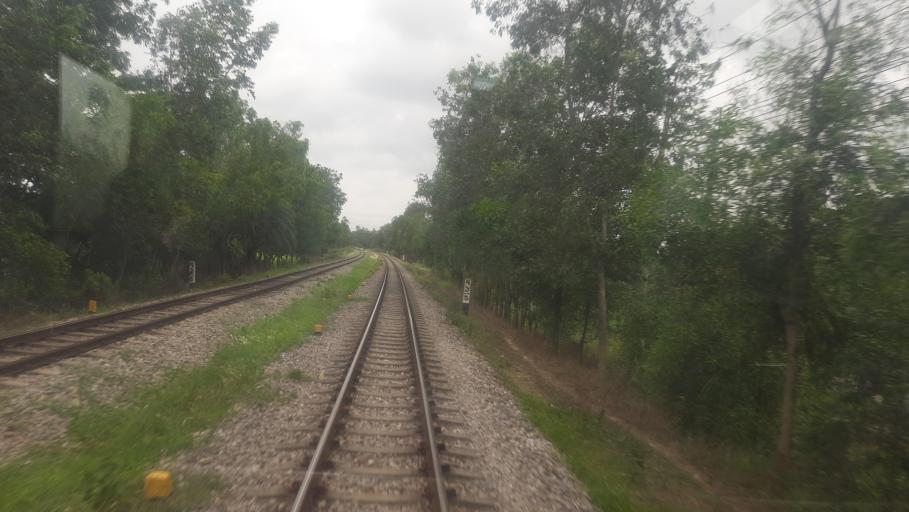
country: BD
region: Chittagong
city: Chhagalnaiya
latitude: 22.9067
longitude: 91.5321
